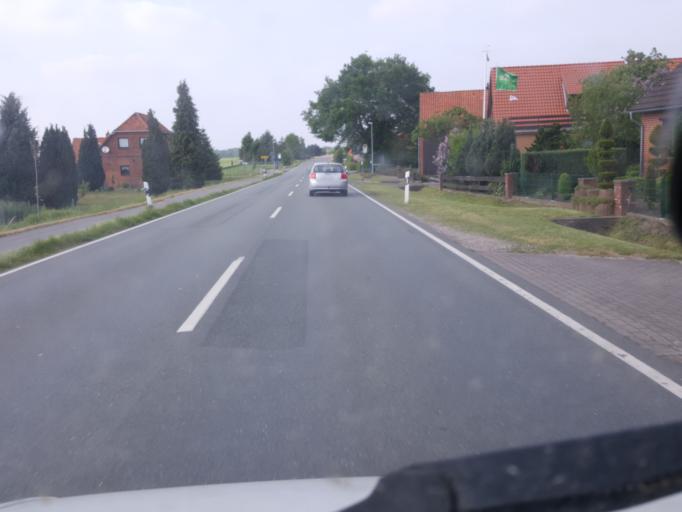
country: DE
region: Lower Saxony
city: Binnen
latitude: 52.6276
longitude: 9.1288
